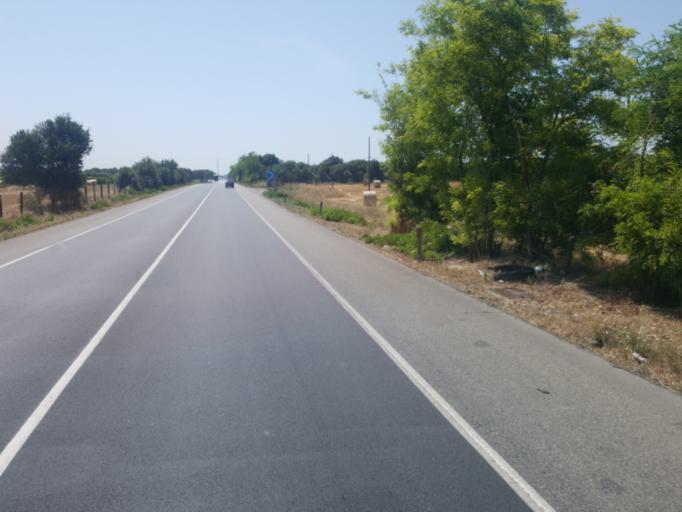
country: IT
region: Apulia
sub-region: Provincia di Taranto
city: Massafra
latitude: 40.5451
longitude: 17.1486
